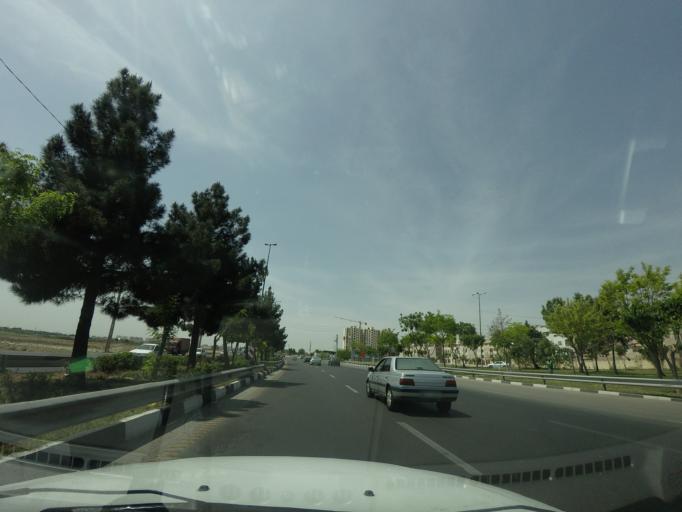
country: IR
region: Tehran
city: Eslamshahr
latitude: 35.5395
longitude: 51.2460
